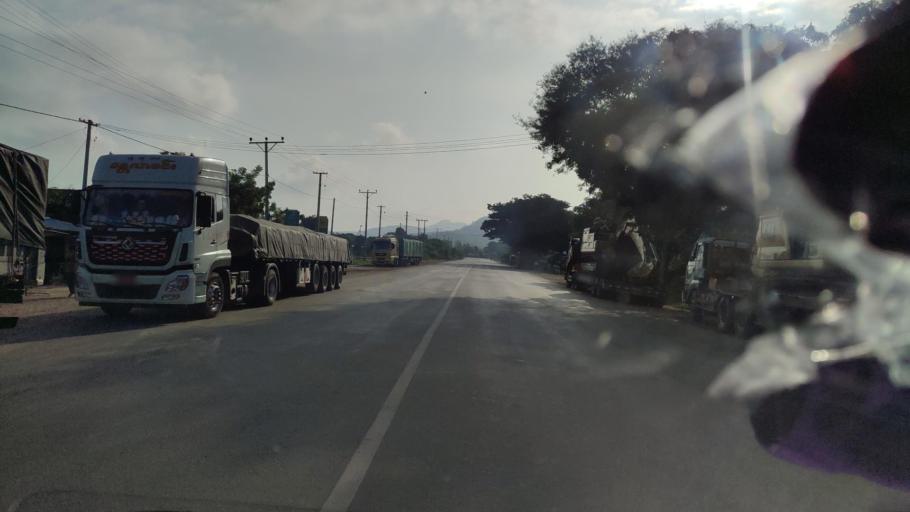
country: MM
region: Mandalay
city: Yamethin
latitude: 20.7525
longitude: 96.2624
